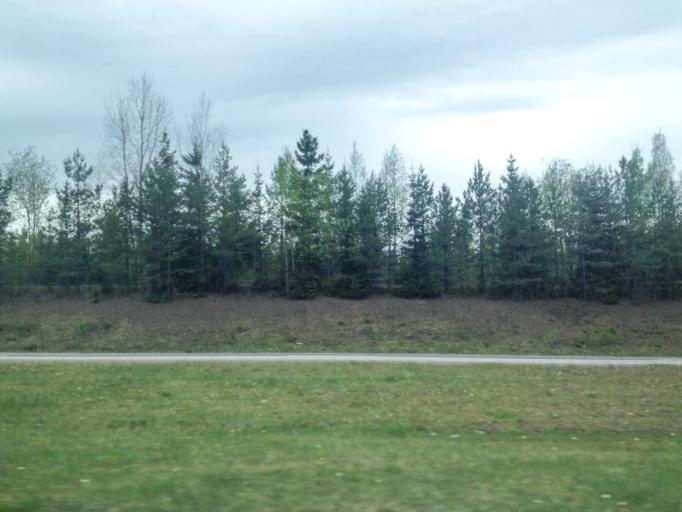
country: FI
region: Uusimaa
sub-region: Helsinki
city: Nurmijaervi
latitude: 60.4707
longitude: 24.8500
